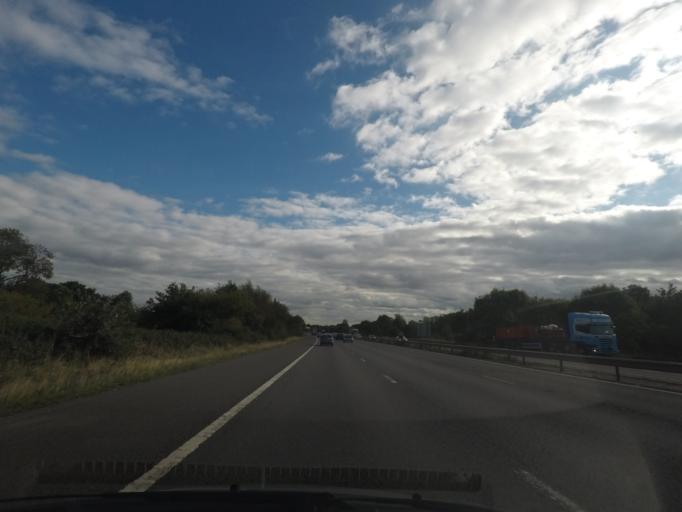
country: GB
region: England
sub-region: Leicestershire
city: Markfield
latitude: 52.6845
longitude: -1.2891
